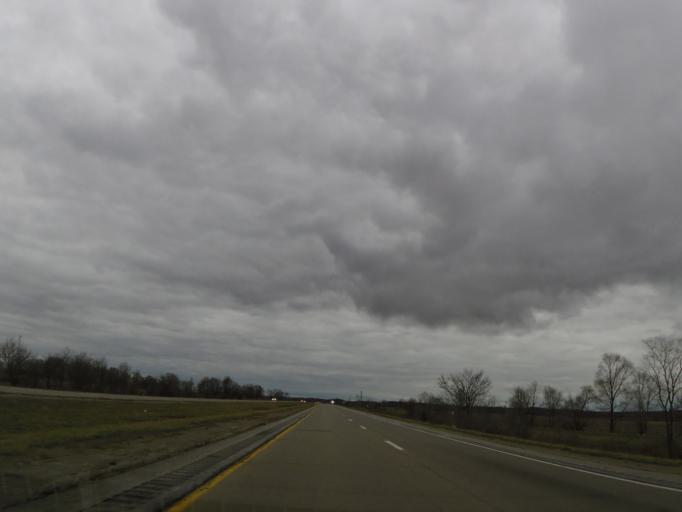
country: US
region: Iowa
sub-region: Johnson County
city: University Heights
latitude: 41.5807
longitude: -91.5456
